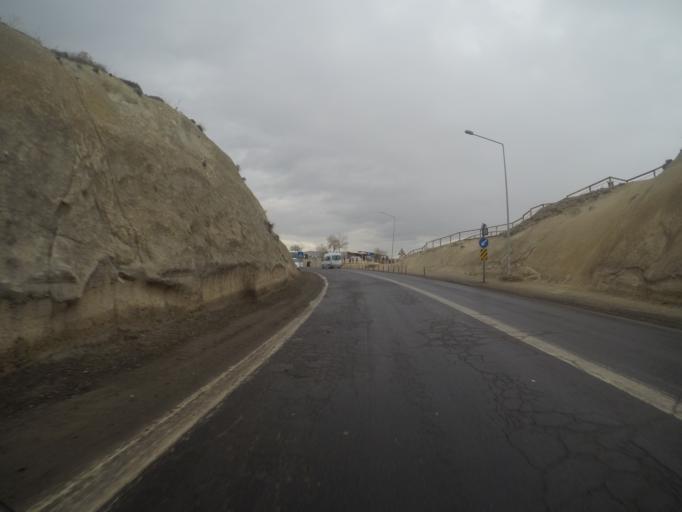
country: TR
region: Nevsehir
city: Urgub
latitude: 38.6349
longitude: 34.8905
